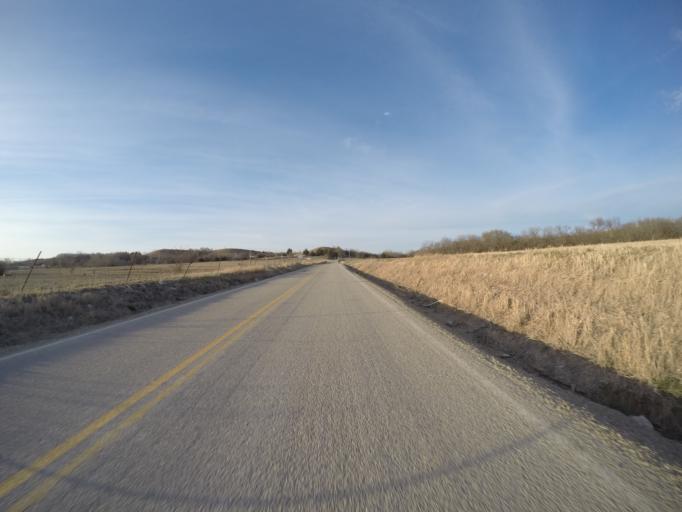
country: US
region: Kansas
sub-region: Riley County
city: Manhattan
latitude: 39.2978
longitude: -96.7002
